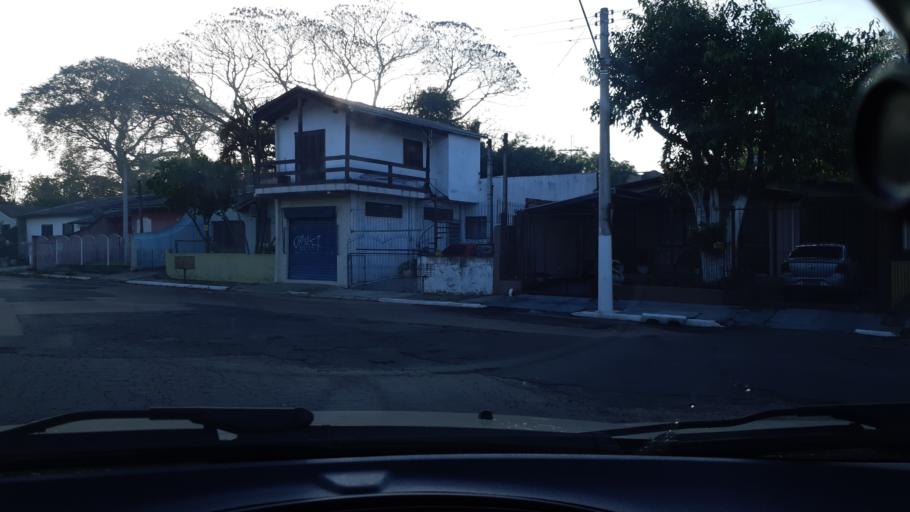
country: BR
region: Rio Grande do Sul
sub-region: Sapucaia Do Sul
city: Sapucaia
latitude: -29.8548
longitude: -51.1363
